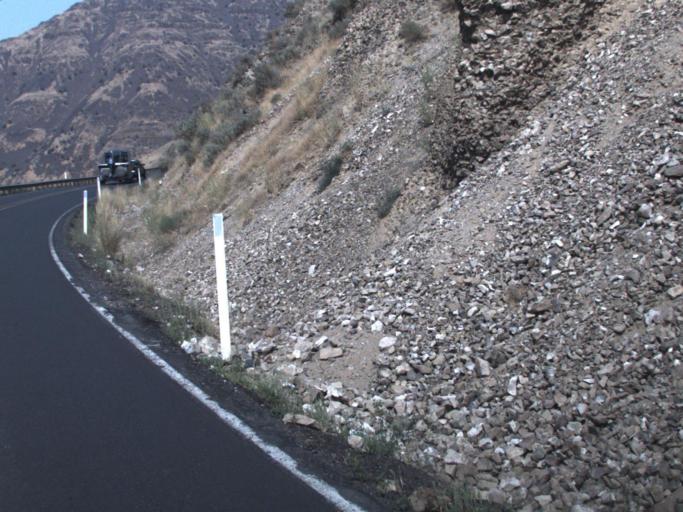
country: US
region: Washington
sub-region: Yakima County
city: Selah
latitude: 46.7327
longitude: -120.4529
